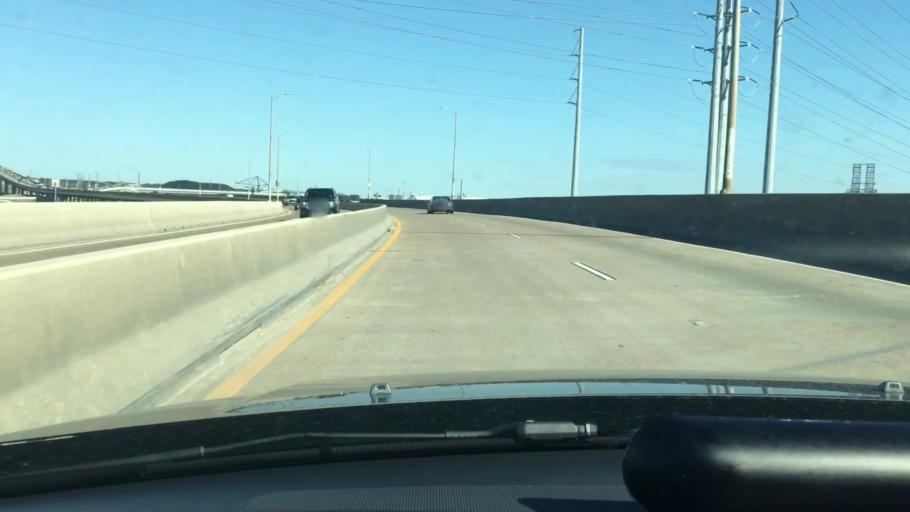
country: US
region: Texas
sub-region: Harris County
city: Deer Park
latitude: 29.7197
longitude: -95.1489
